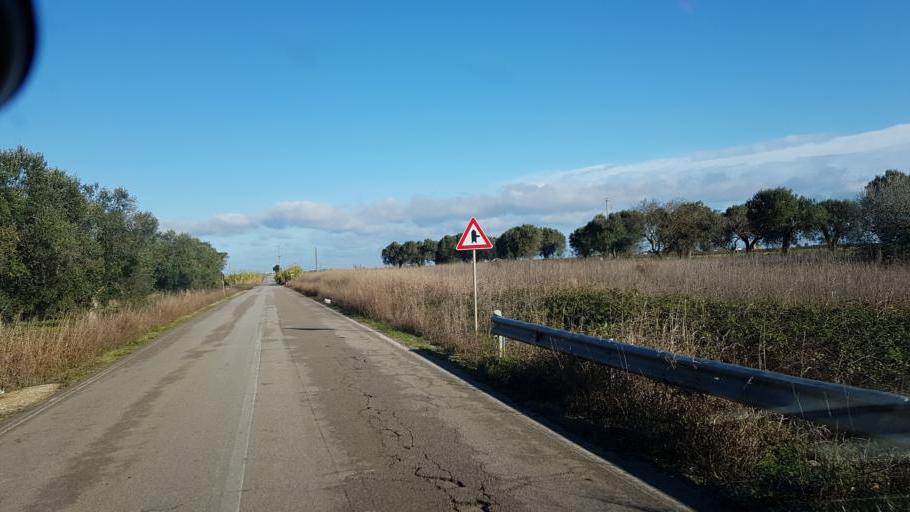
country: IT
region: Apulia
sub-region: Provincia di Brindisi
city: Tuturano
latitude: 40.5669
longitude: 17.9492
